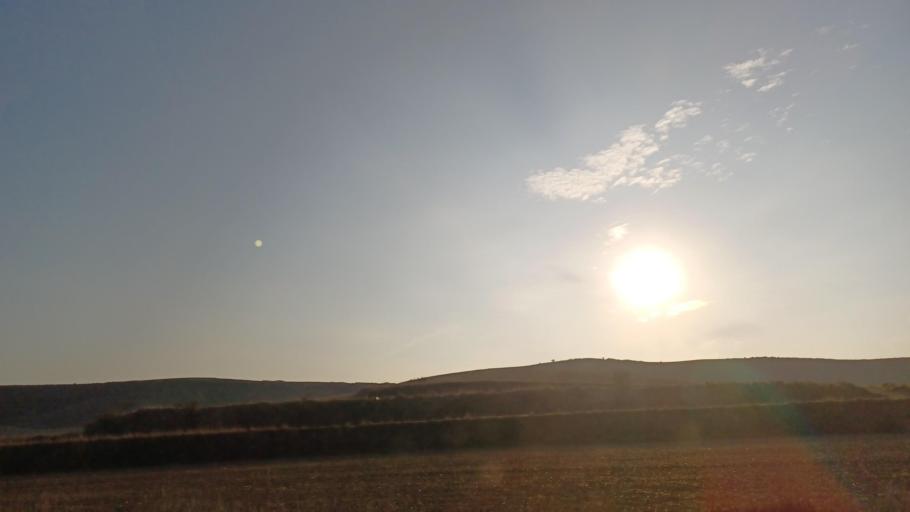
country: CY
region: Lefkosia
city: Lympia
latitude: 35.0378
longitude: 33.4952
